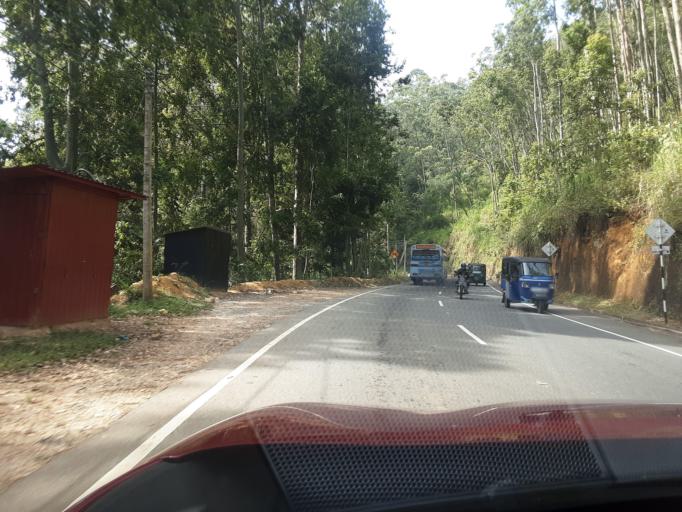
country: LK
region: Uva
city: Badulla
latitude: 6.9636
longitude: 81.0957
